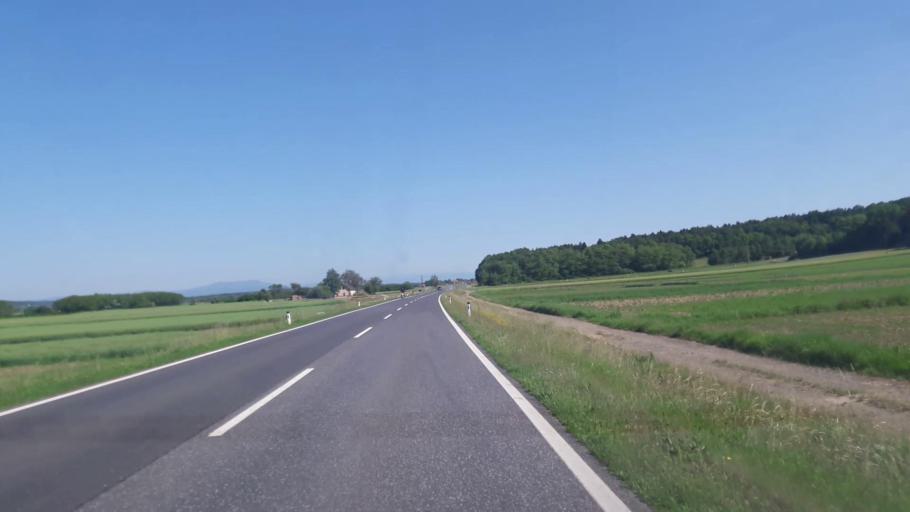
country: AT
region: Burgenland
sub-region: Politischer Bezirk Jennersdorf
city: Rudersdorf
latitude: 47.0644
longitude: 16.1148
